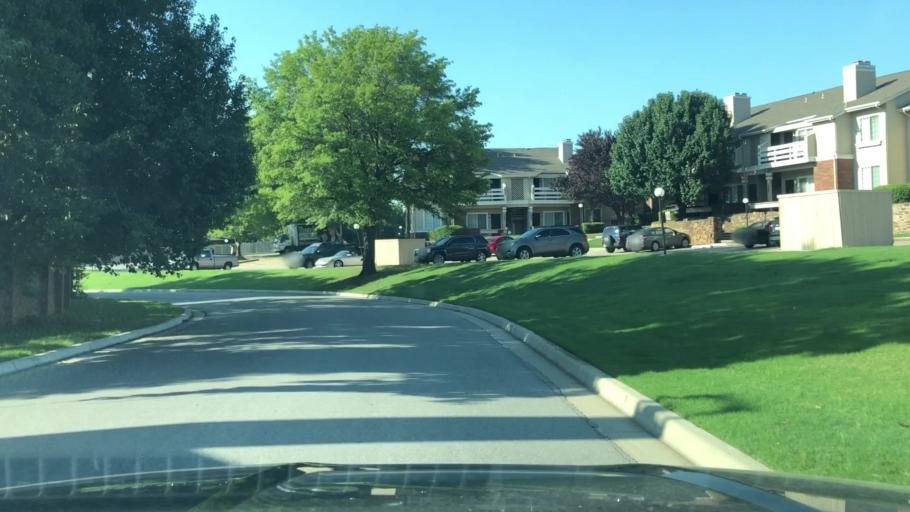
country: US
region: Oklahoma
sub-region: Tulsa County
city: Jenks
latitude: 36.0314
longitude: -95.9005
